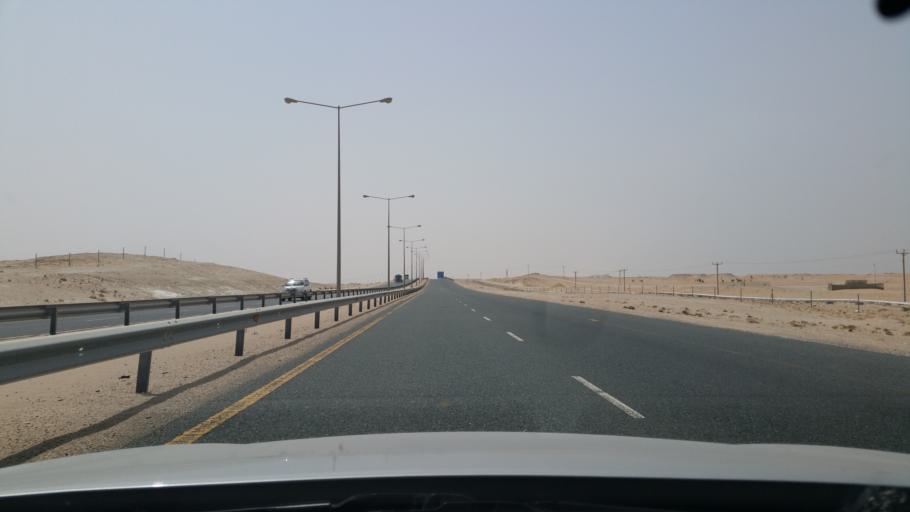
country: QA
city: Umm Bab
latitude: 25.1746
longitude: 50.8110
